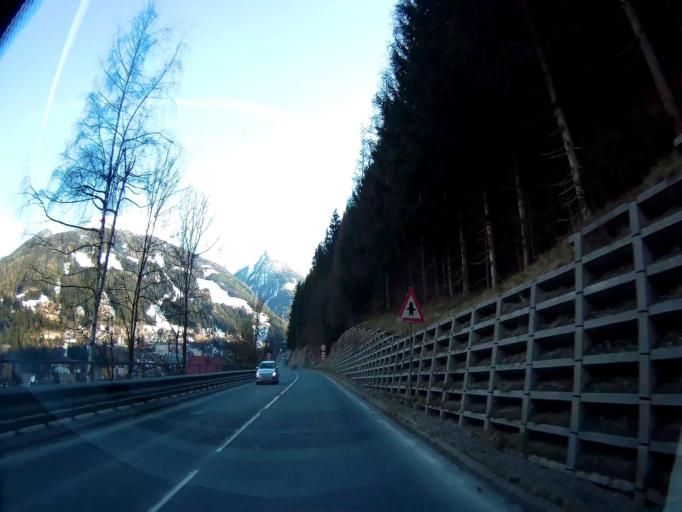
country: AT
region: Salzburg
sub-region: Politischer Bezirk Sankt Johann im Pongau
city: Bad Gastein
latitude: 47.1315
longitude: 13.1290
